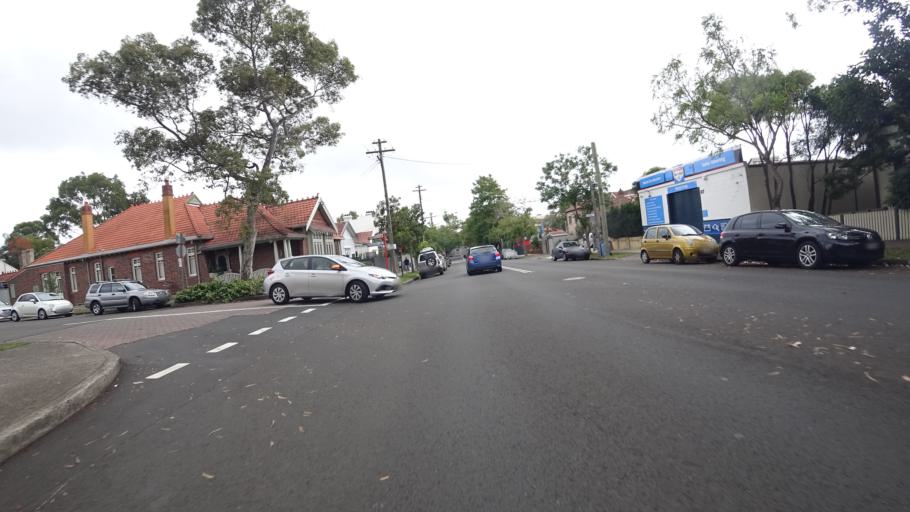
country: AU
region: New South Wales
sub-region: North Sydney
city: Crows Nest
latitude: -33.8296
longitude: 151.2061
